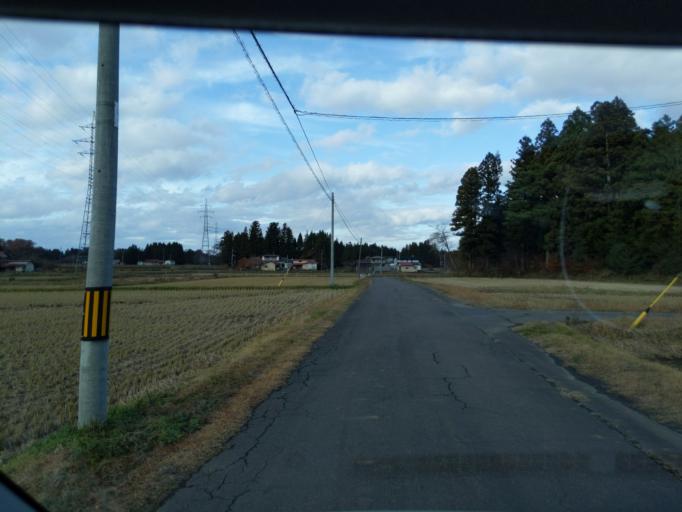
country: JP
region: Iwate
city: Mizusawa
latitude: 39.1062
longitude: 141.0877
